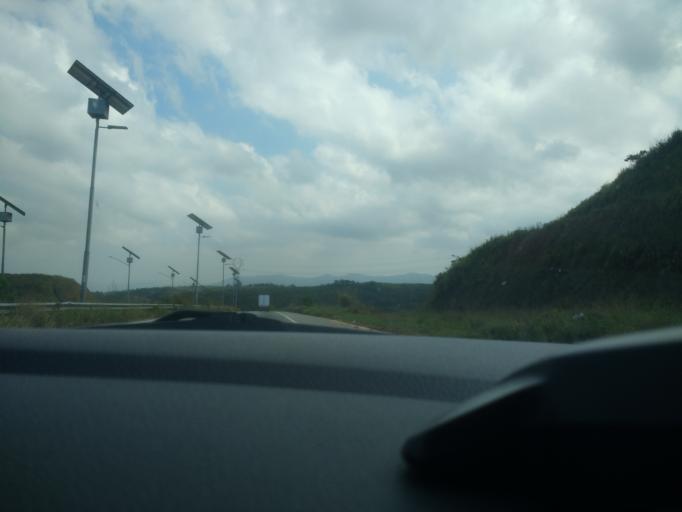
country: BR
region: Rio de Janeiro
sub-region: Queimados
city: Queimados
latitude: -22.6825
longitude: -43.5272
